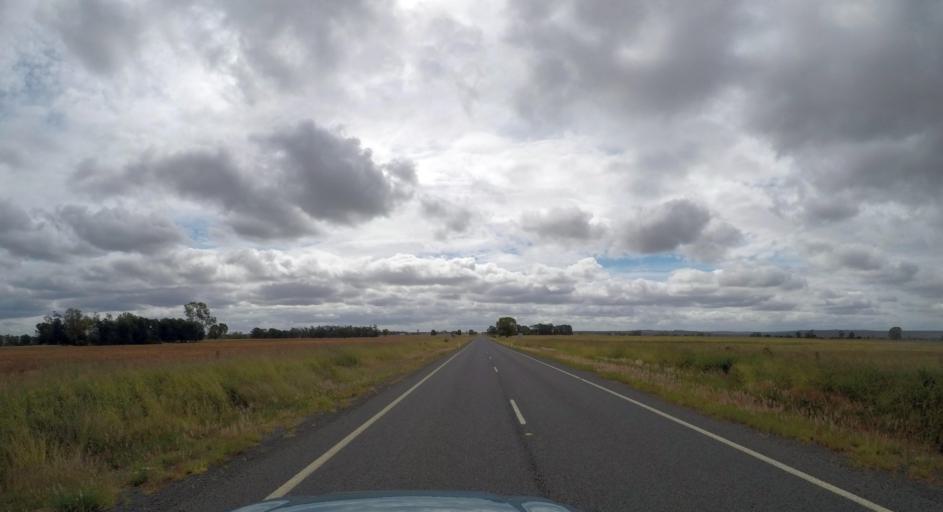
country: AU
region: Queensland
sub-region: South Burnett
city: Kingaroy
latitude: -26.3895
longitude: 151.2445
